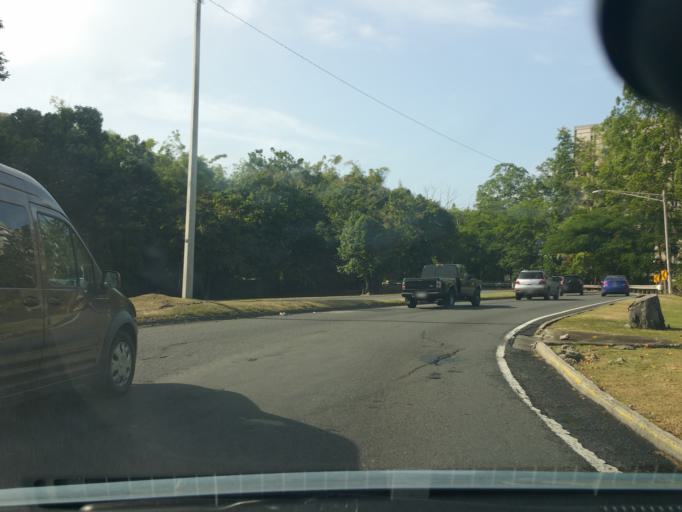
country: PR
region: Catano
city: Catano
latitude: 18.4078
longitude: -66.0681
